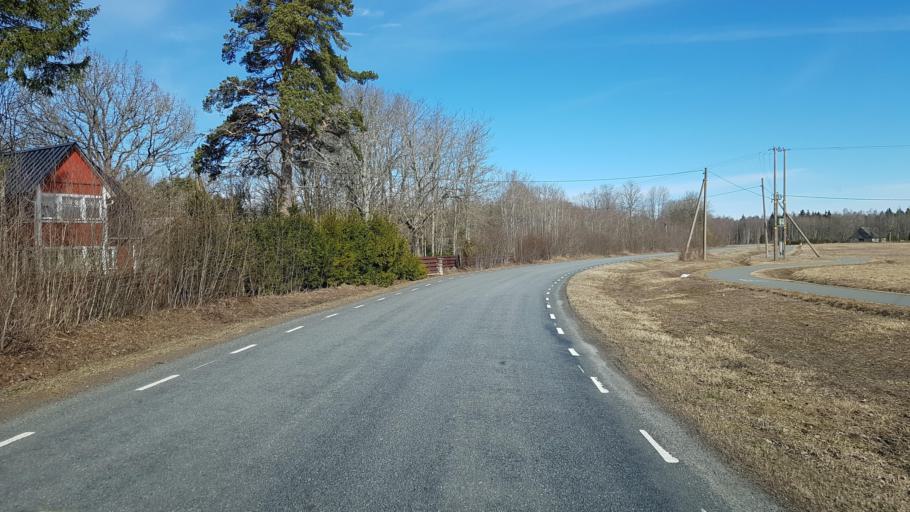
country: EE
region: Harju
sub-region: Nissi vald
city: Riisipere
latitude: 59.2368
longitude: 24.2440
